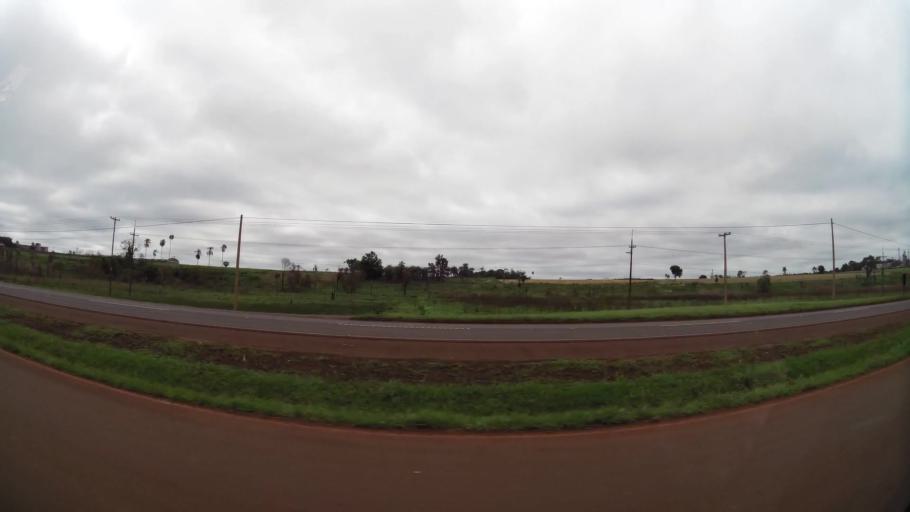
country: PY
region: Alto Parana
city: Colonia Yguazu
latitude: -25.4881
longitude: -54.8284
